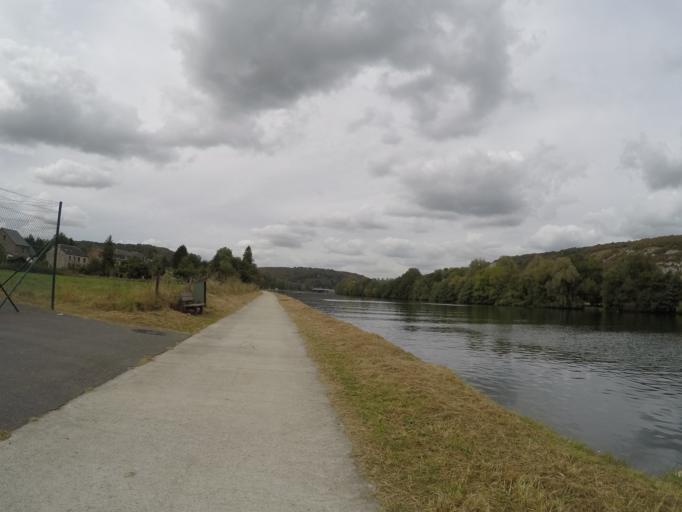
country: BE
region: Wallonia
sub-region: Province de Namur
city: Anhee
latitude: 50.3080
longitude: 4.8869
